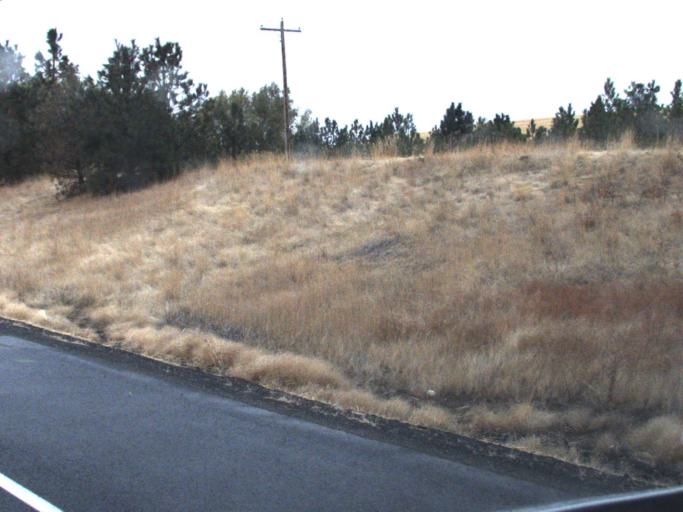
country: US
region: Washington
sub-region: Whitman County
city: Pullman
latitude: 46.7490
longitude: -117.2354
